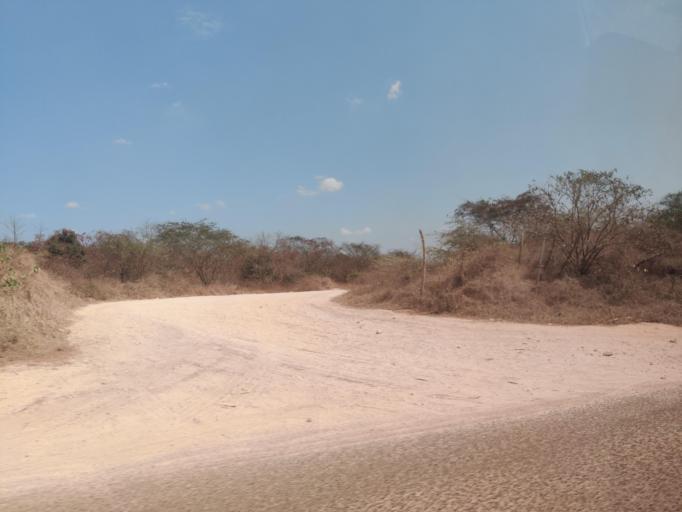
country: CO
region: Bolivar
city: Turbana
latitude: 10.2760
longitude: -75.5221
